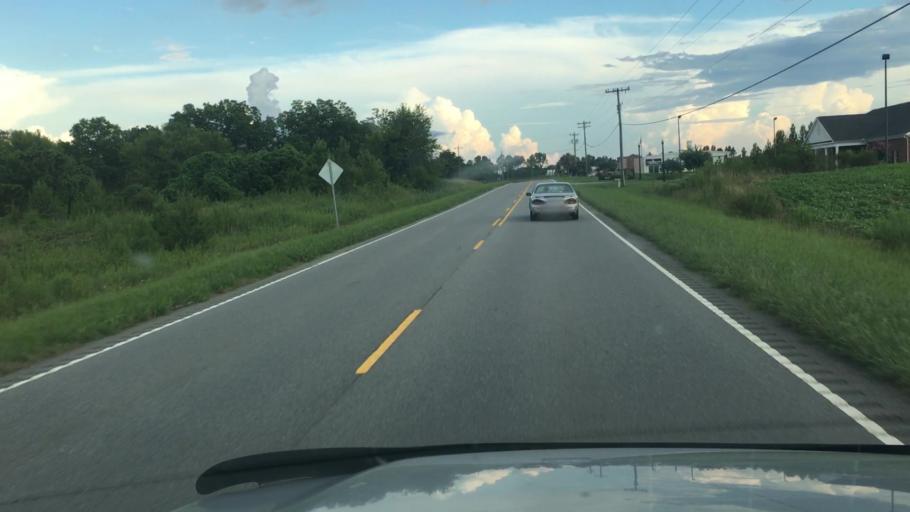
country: US
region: South Carolina
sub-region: Cherokee County
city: Gaffney
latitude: 35.1087
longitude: -81.6985
